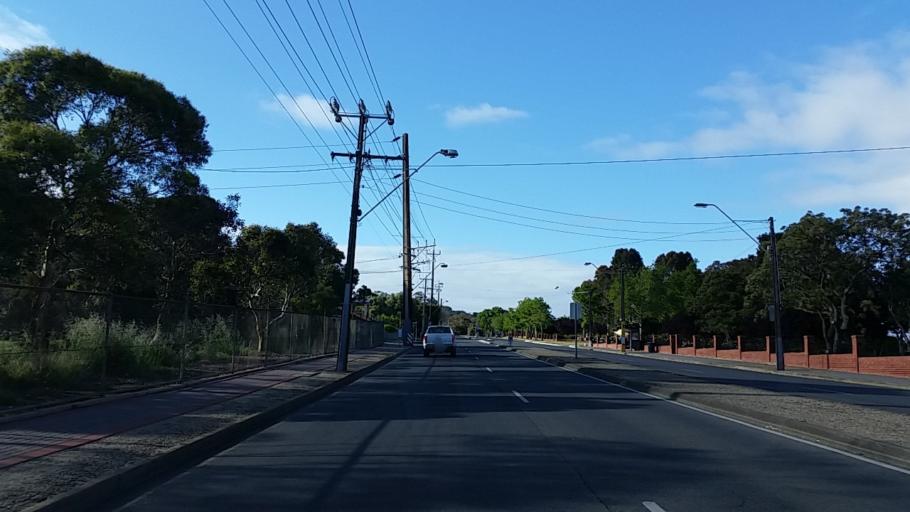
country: AU
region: South Australia
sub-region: Mitcham
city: Clapham
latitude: -34.9955
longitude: 138.5931
